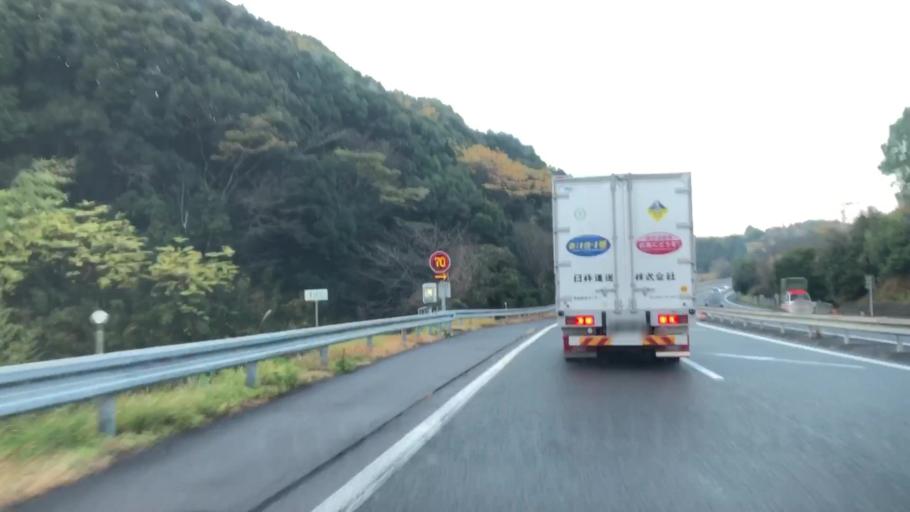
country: JP
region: Nagasaki
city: Sasebo
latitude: 33.1550
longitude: 129.8126
